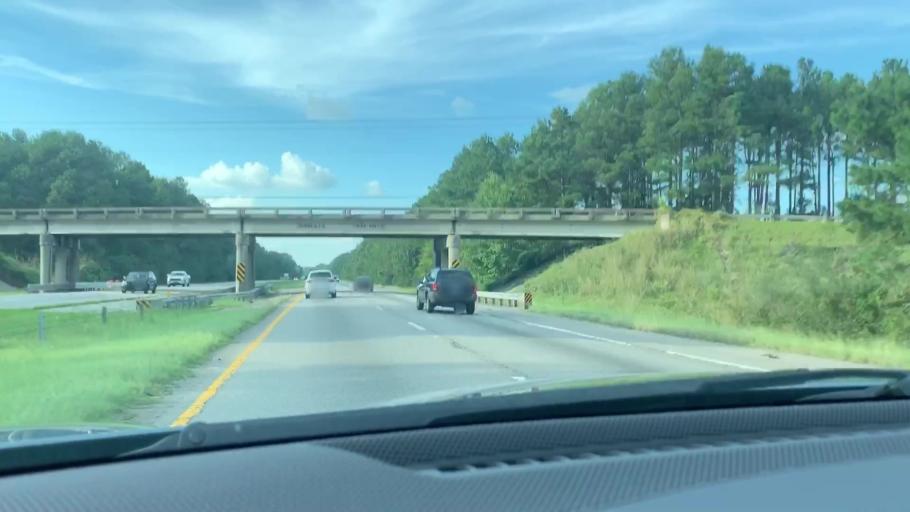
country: US
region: South Carolina
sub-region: Orangeburg County
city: Brookdale
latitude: 33.4858
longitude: -80.7596
